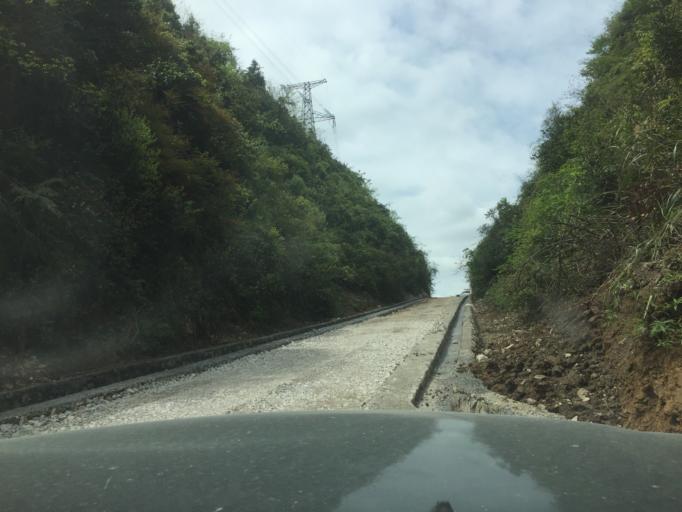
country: CN
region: Guizhou Sheng
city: Jiancha
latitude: 28.1955
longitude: 107.9845
